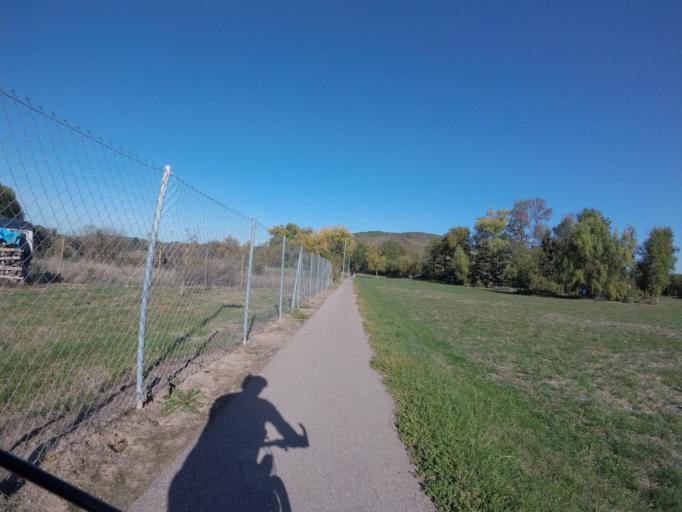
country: DE
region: Baden-Wuerttemberg
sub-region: Regierungsbezirk Stuttgart
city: Sersheim
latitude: 48.9810
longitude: 8.9863
